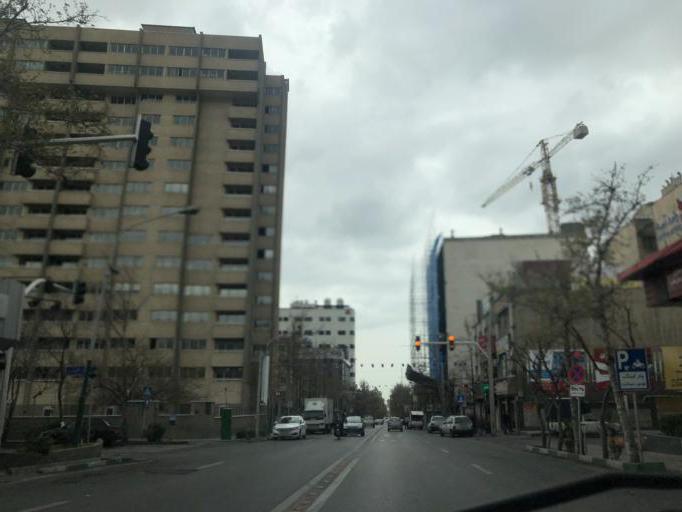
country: IR
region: Tehran
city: Tajrish
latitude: 35.7752
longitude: 51.4642
